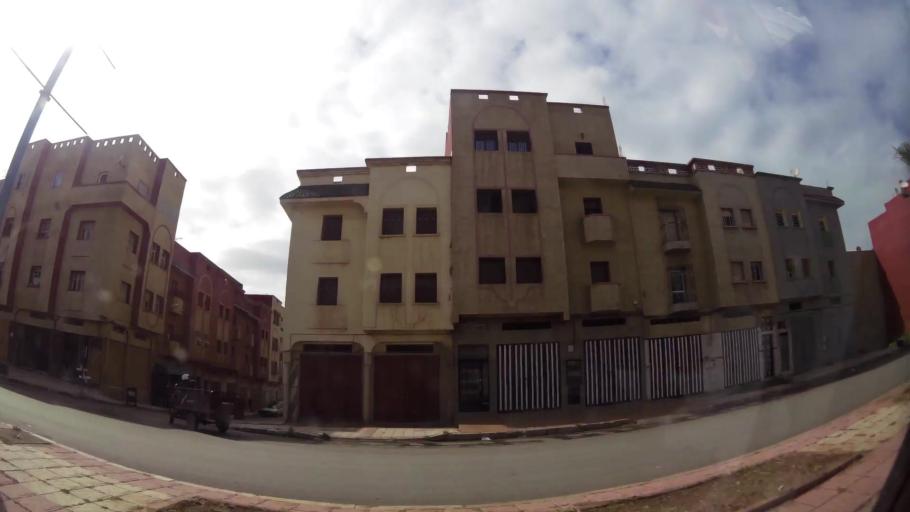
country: MA
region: Grand Casablanca
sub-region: Mohammedia
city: Mohammedia
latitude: 33.6740
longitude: -7.3928
